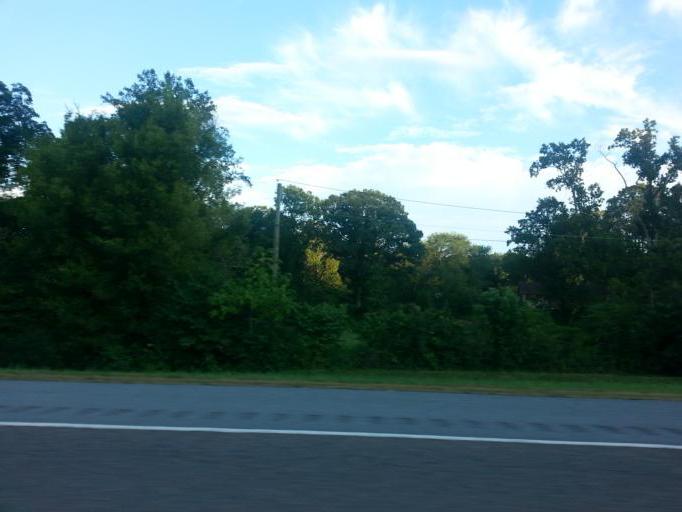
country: US
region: Tennessee
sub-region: Knox County
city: Mascot
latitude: 36.0980
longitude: -83.7487
